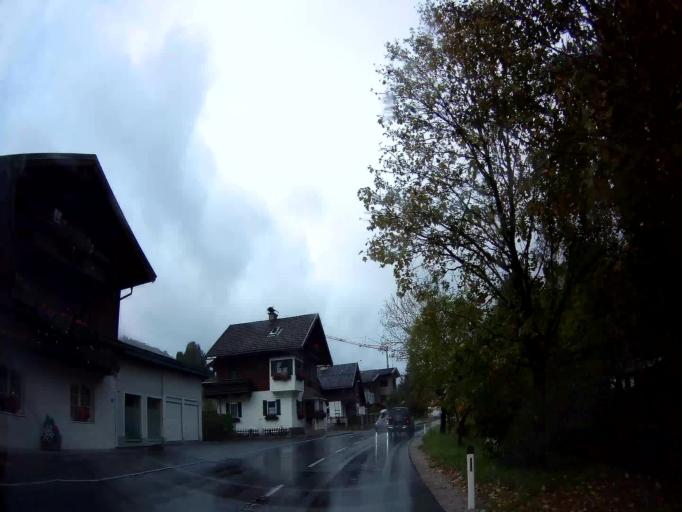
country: AT
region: Salzburg
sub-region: Politischer Bezirk Zell am See
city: Leogang
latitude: 47.4388
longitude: 12.7536
